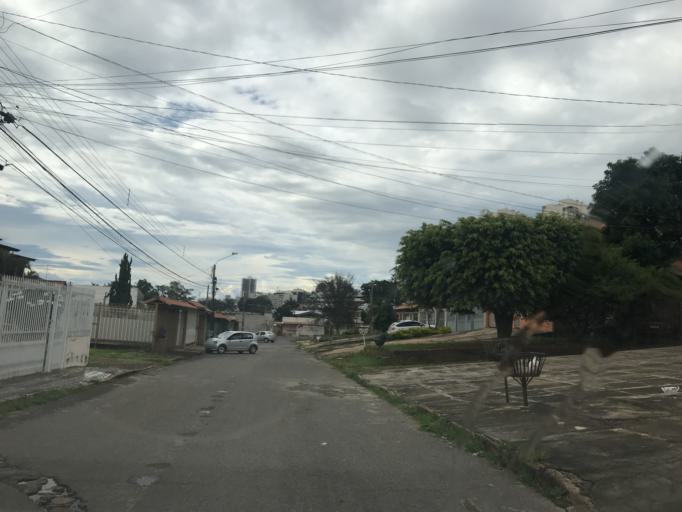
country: BR
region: Federal District
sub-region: Brasilia
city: Brasilia
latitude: -15.8455
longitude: -48.0513
